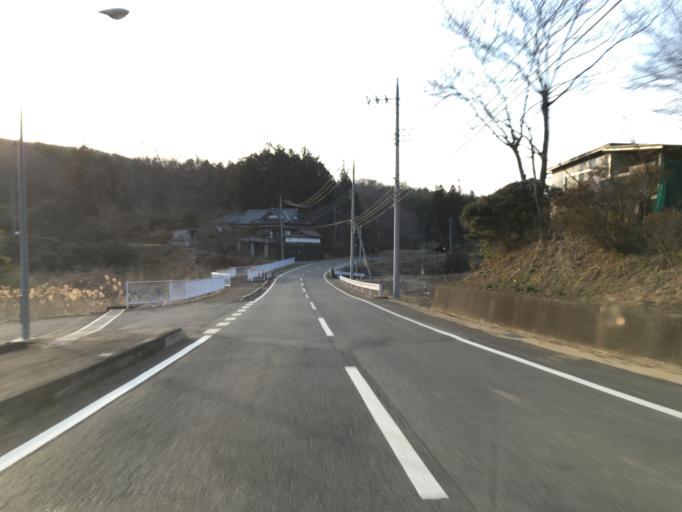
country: JP
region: Ibaraki
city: Daigo
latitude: 36.7901
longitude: 140.4151
